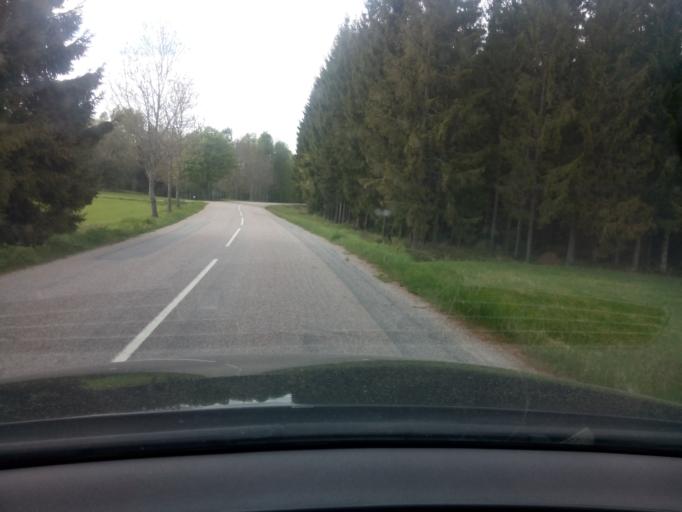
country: SE
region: Soedermanland
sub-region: Nykopings Kommun
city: Nykoping
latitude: 58.8417
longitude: 16.9336
